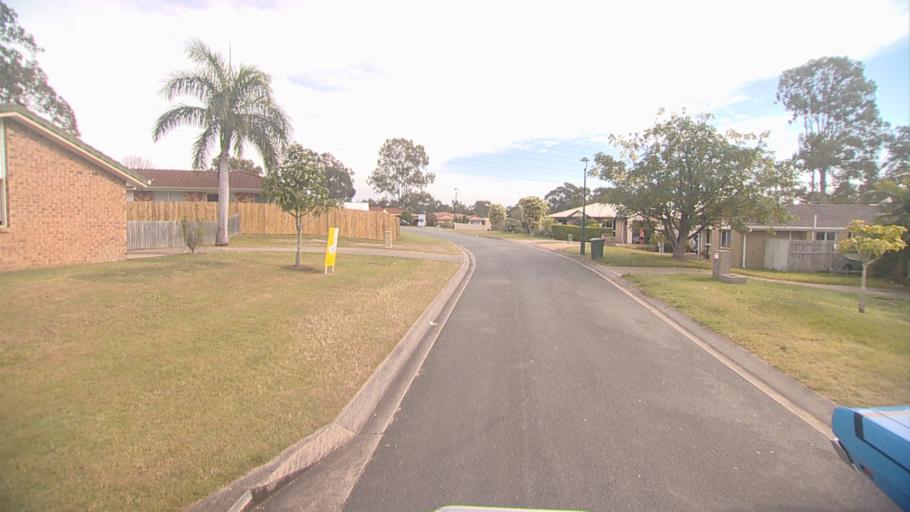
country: AU
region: Queensland
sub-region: Logan
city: Beenleigh
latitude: -27.7012
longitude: 153.1780
